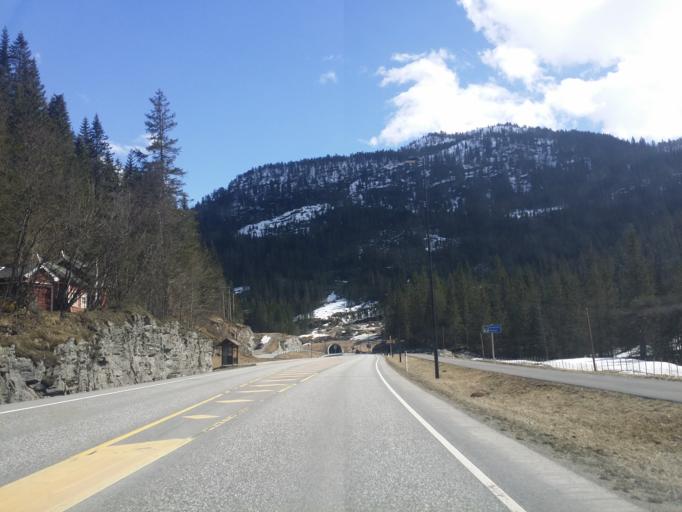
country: NO
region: Hordaland
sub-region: Granvin
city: Granvin
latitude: 60.5873
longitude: 6.6077
